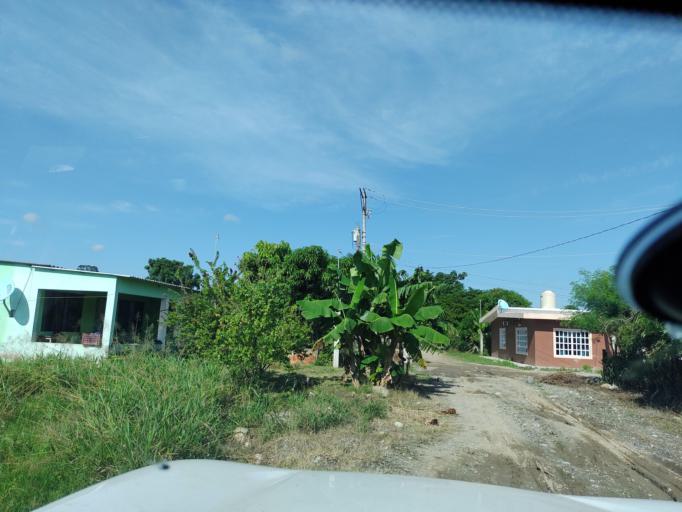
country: MX
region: Veracruz
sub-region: Martinez de la Torre
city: El Progreso
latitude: 20.1107
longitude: -96.9877
